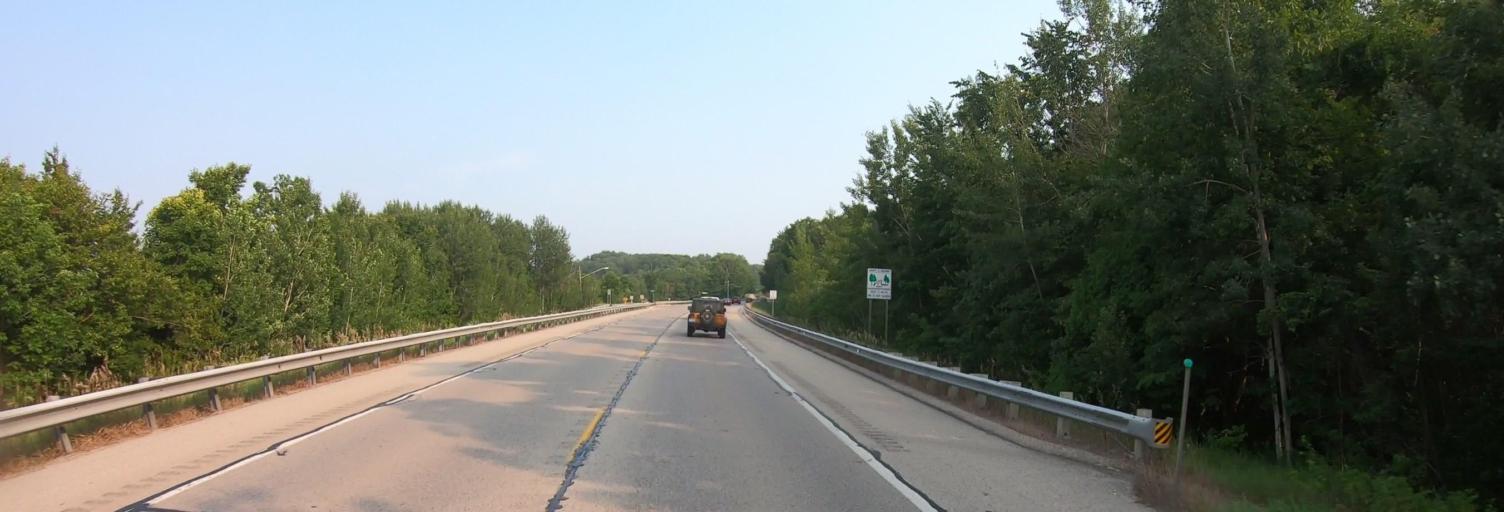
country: US
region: Michigan
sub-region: Charlevoix County
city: Charlevoix
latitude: 45.3661
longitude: -85.1238
